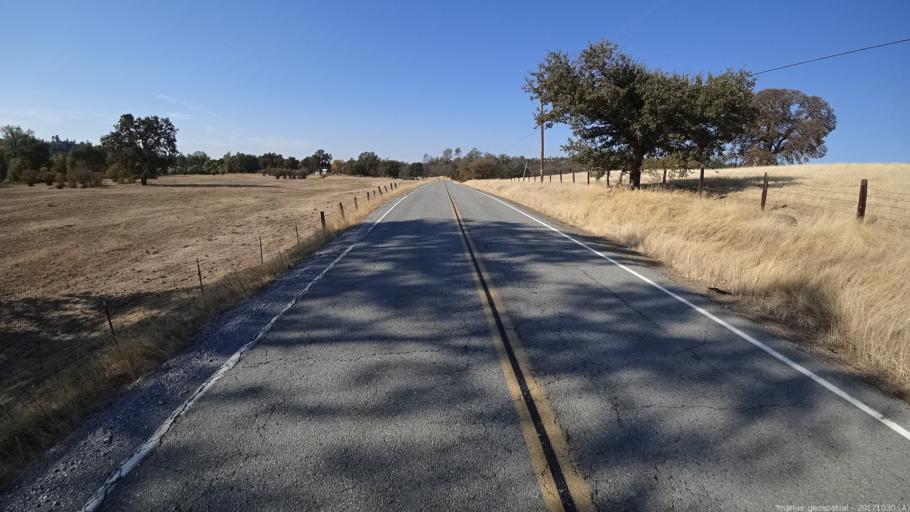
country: US
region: California
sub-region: Shasta County
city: Bella Vista
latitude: 40.6121
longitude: -122.1414
